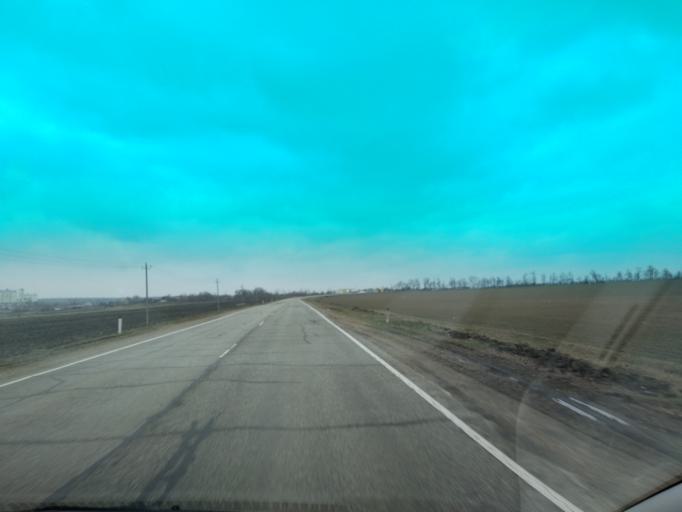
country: RU
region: Krasnodarskiy
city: Novomalorossiyskaya
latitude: 45.7113
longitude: 39.8673
